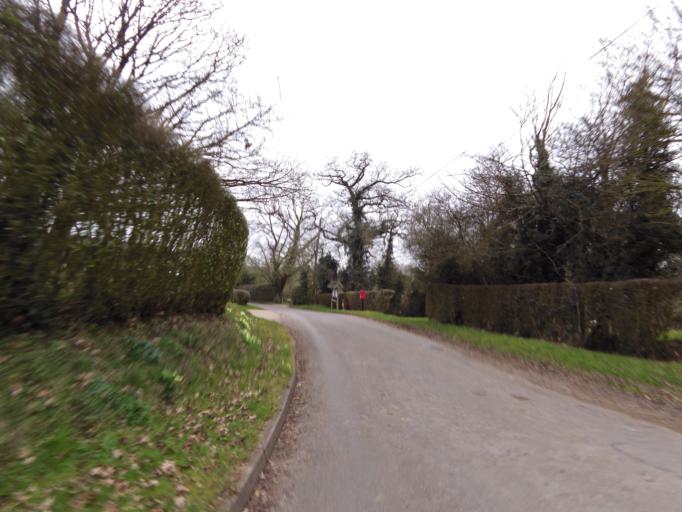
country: GB
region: England
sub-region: Suffolk
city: Framlingham
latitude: 52.2464
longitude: 1.4079
